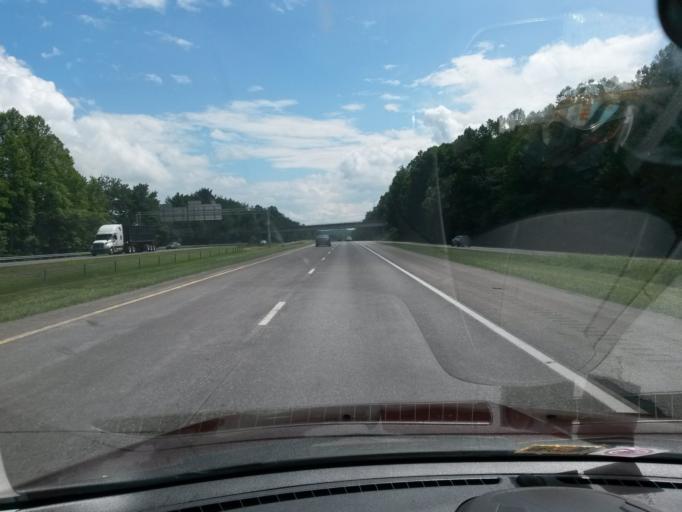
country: US
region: North Carolina
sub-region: Surry County
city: Dobson
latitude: 36.4806
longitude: -80.7522
